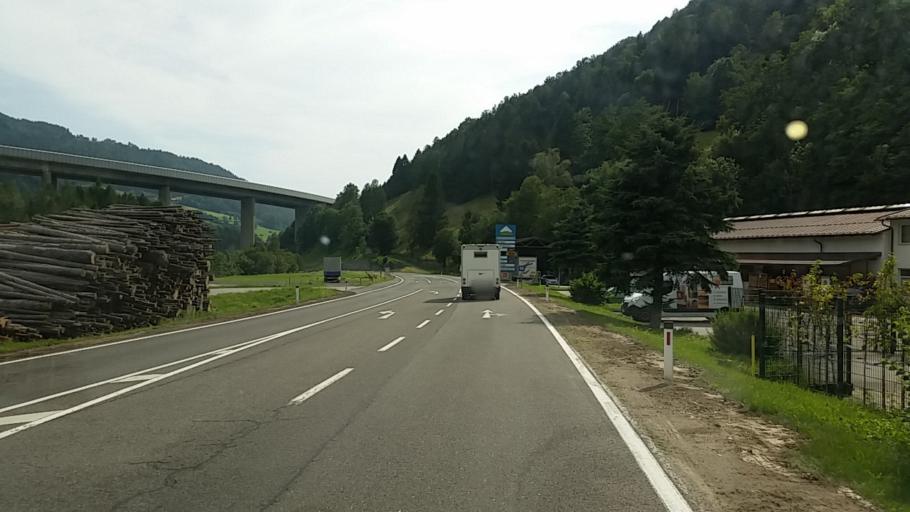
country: AT
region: Carinthia
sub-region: Politischer Bezirk Spittal an der Drau
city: Gmuend
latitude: 46.9031
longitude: 13.5306
